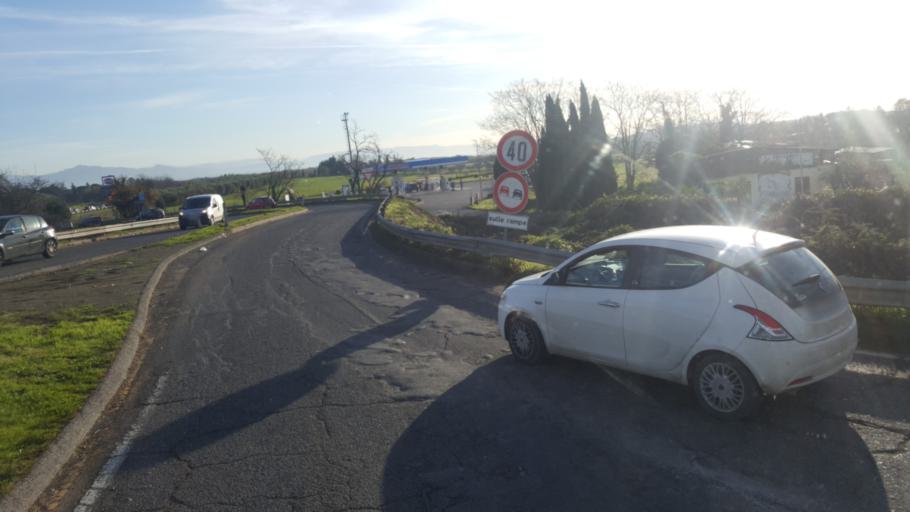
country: IT
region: Latium
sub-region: Citta metropolitana di Roma Capitale
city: Formello
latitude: 42.0449
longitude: 12.3948
